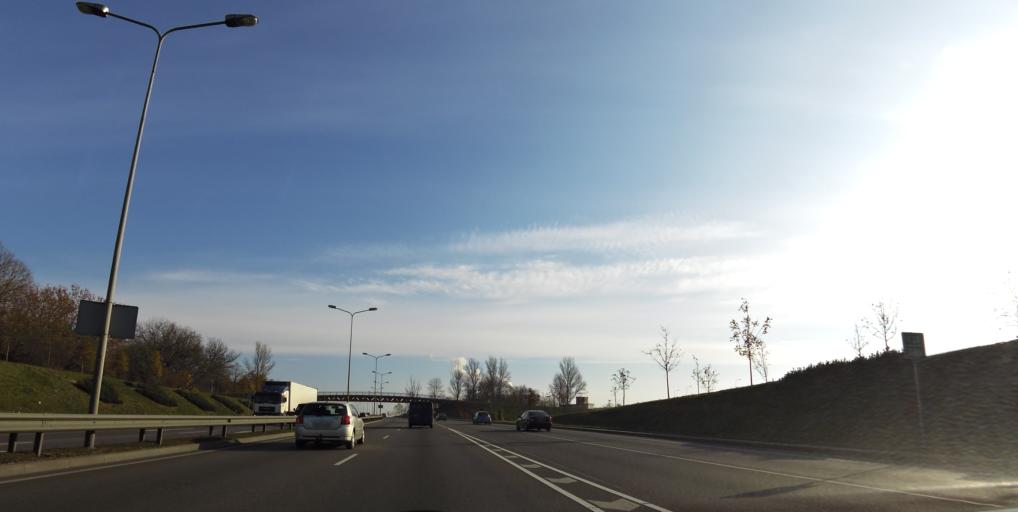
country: LT
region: Vilnius County
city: Vilkpede
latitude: 54.6673
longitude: 25.2441
